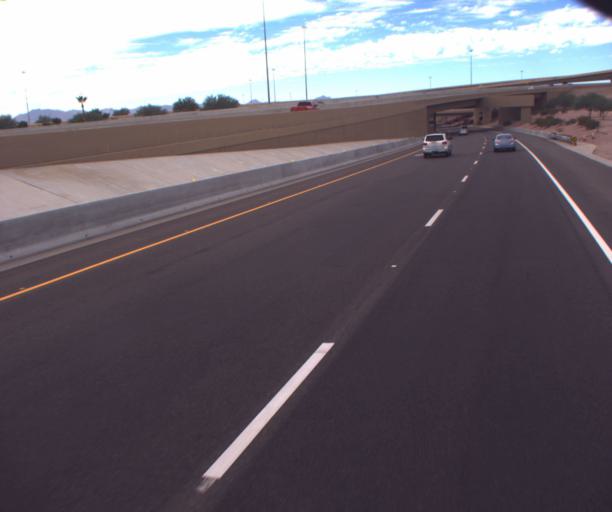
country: US
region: Arizona
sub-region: Maricopa County
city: Guadalupe
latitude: 33.2968
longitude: -111.9681
